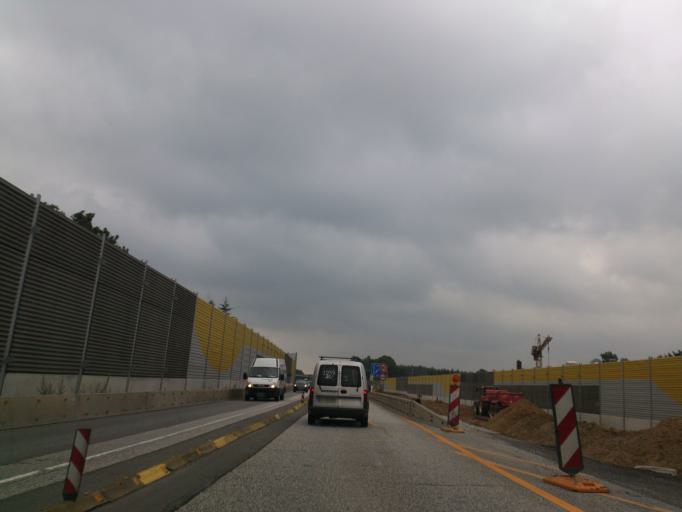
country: DE
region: Schleswig-Holstein
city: Itzehoe
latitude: 53.9019
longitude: 9.4989
